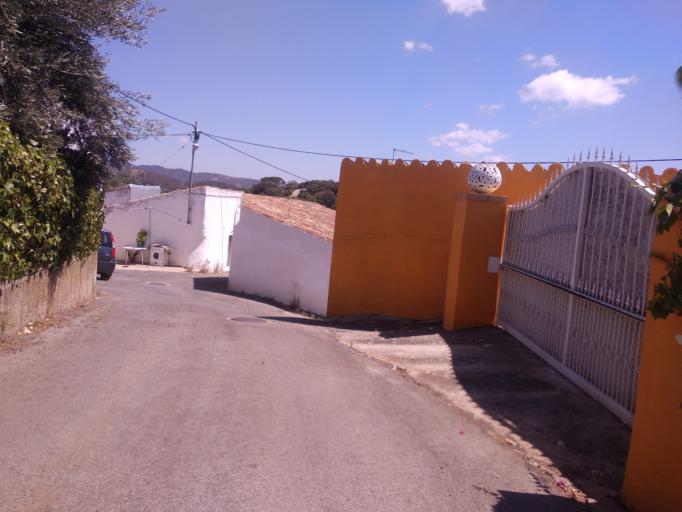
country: PT
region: Faro
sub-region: Sao Bras de Alportel
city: Sao Bras de Alportel
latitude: 37.1609
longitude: -7.9013
